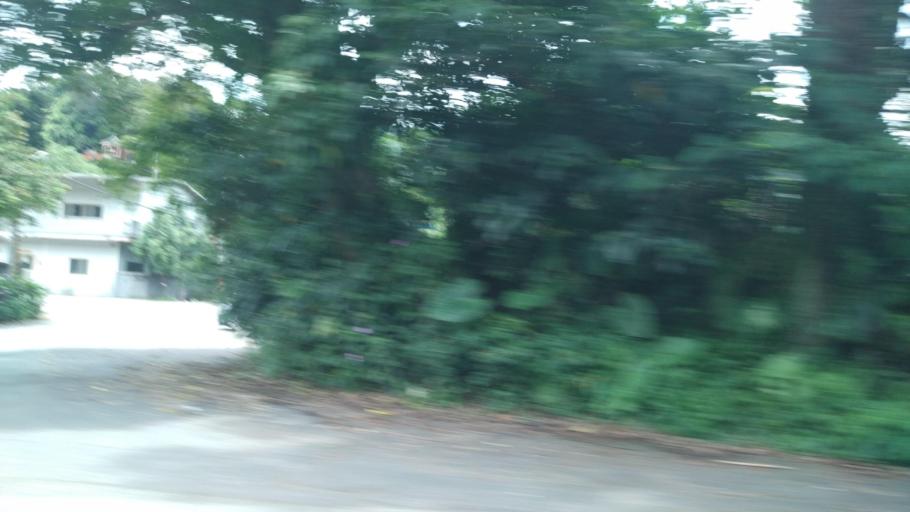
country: TW
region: Taipei
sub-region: Taipei
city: Banqiao
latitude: 24.9412
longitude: 121.4725
